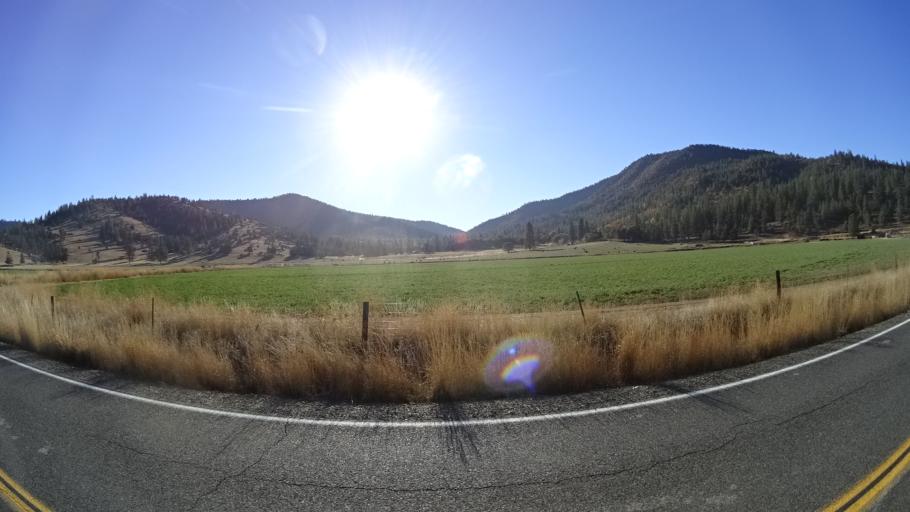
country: US
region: California
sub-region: Siskiyou County
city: Yreka
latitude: 41.5384
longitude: -122.8325
